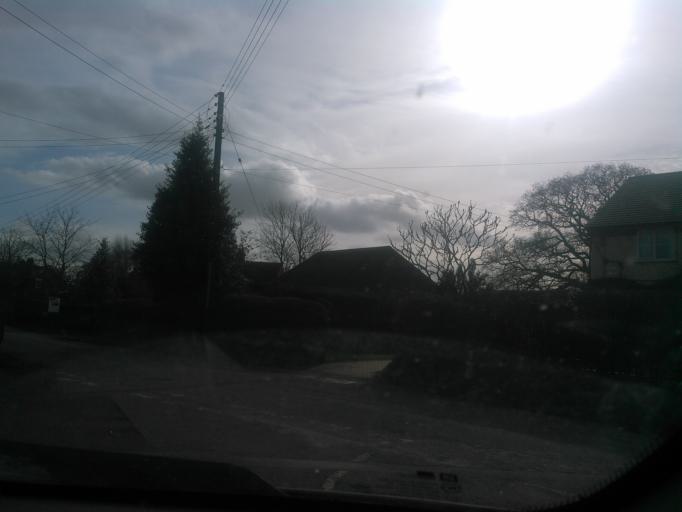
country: GB
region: England
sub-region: Shropshire
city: Bicton
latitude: 52.7716
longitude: -2.7766
